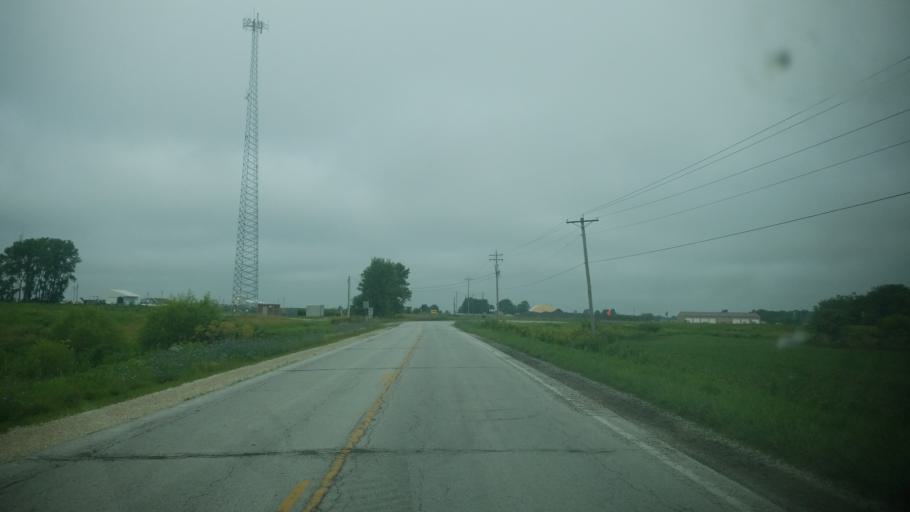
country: US
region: Missouri
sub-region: Pike County
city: Bowling Green
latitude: 39.3445
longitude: -91.2304
